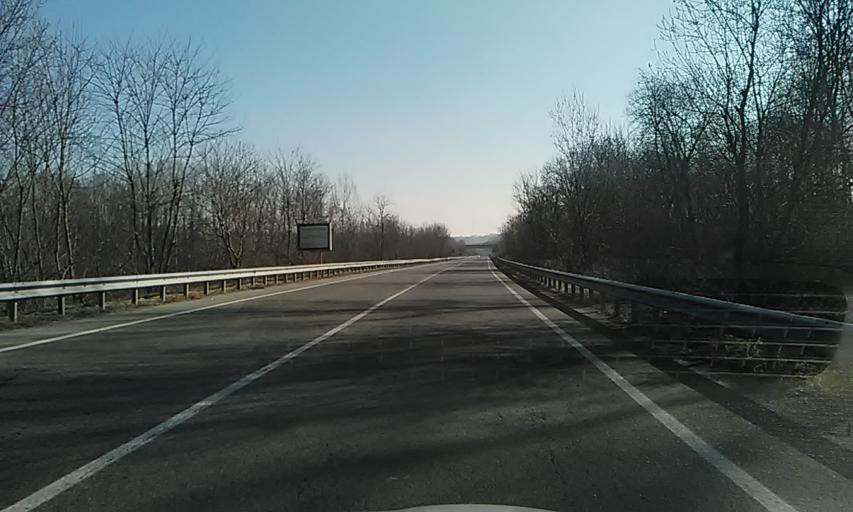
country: IT
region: Piedmont
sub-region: Provincia di Novara
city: Prato Sesia
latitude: 45.6671
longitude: 8.3619
